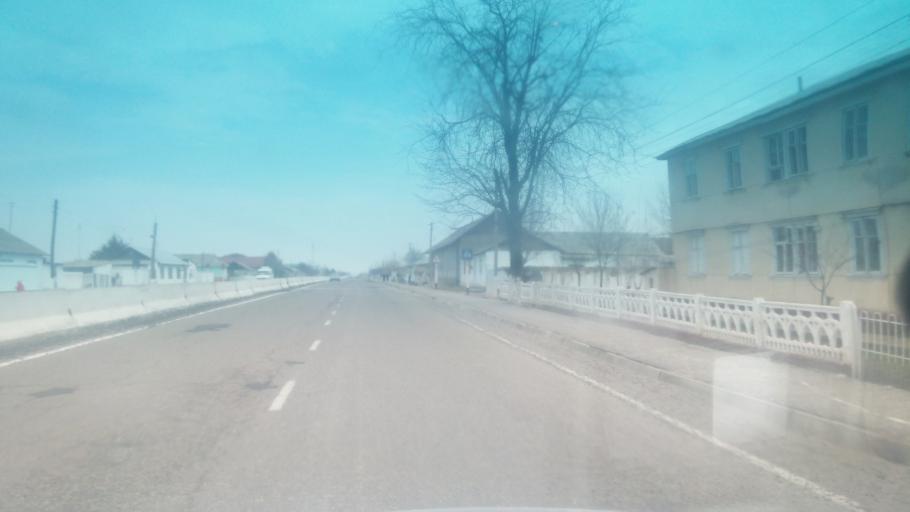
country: KZ
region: Ongtustik Qazaqstan
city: Myrzakent
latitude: 40.4999
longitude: 68.5663
